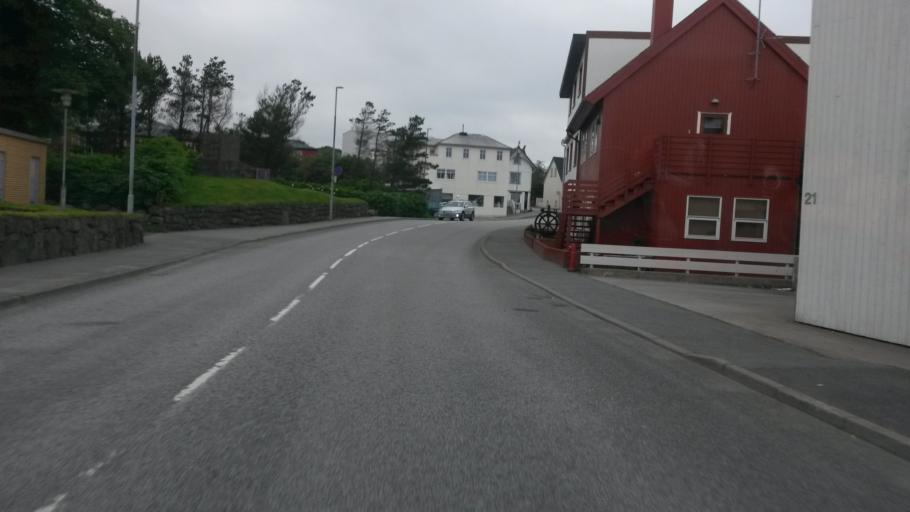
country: FO
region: Streymoy
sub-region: Torshavn
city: Torshavn
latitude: 62.0072
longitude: -6.7777
